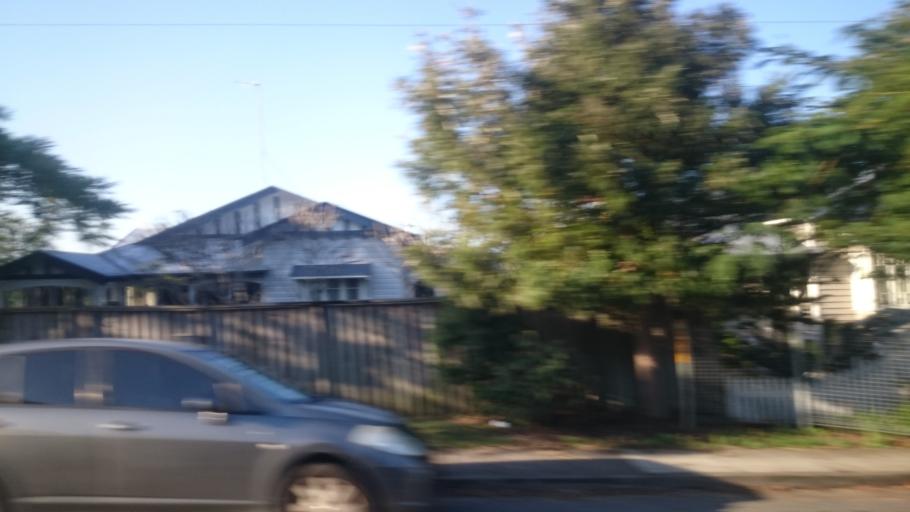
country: AU
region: Queensland
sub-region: Brisbane
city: Wynnum
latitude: -27.4483
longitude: 153.1781
